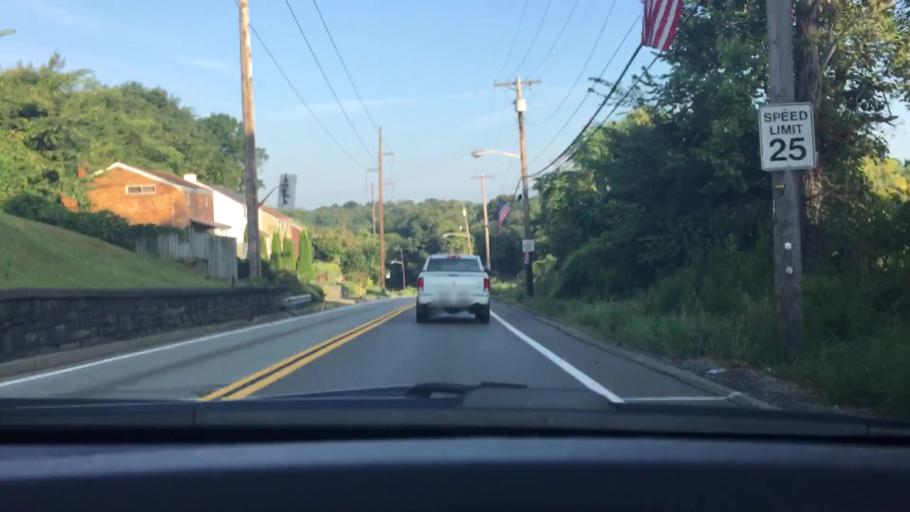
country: US
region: Pennsylvania
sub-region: Allegheny County
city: West Homestead
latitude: 40.3704
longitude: -79.9141
